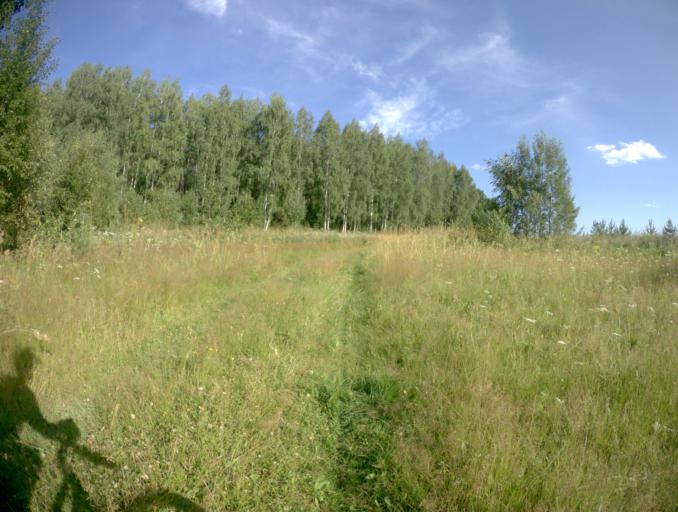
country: RU
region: Vladimir
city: Bogolyubovo
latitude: 56.1210
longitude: 40.5343
